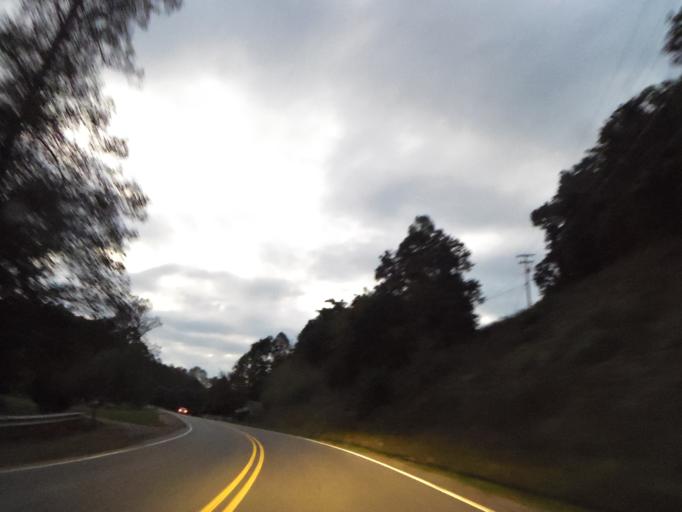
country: US
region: North Carolina
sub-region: Madison County
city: Marshall
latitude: 35.8884
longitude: -82.7442
